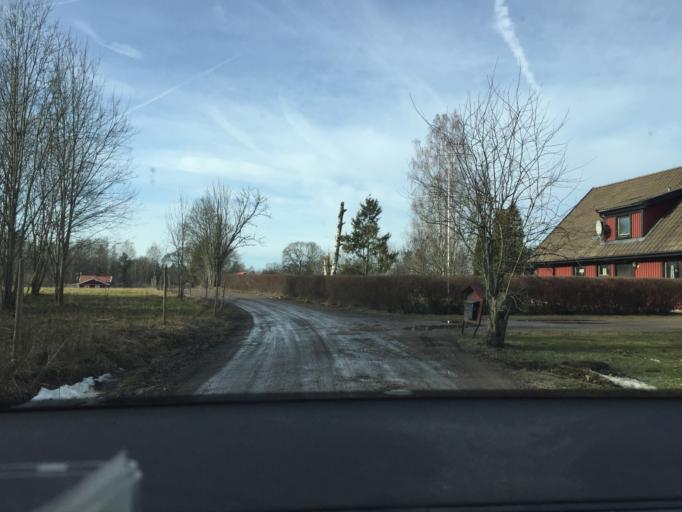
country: SE
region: OErebro
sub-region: Orebro Kommun
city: Odensbacken
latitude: 59.1154
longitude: 15.4621
